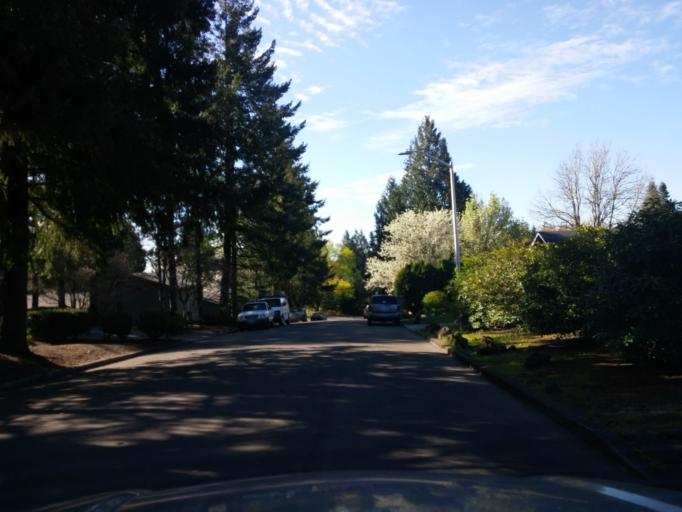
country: US
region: Oregon
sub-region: Washington County
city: Cedar Mill
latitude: 45.5407
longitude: -122.7908
